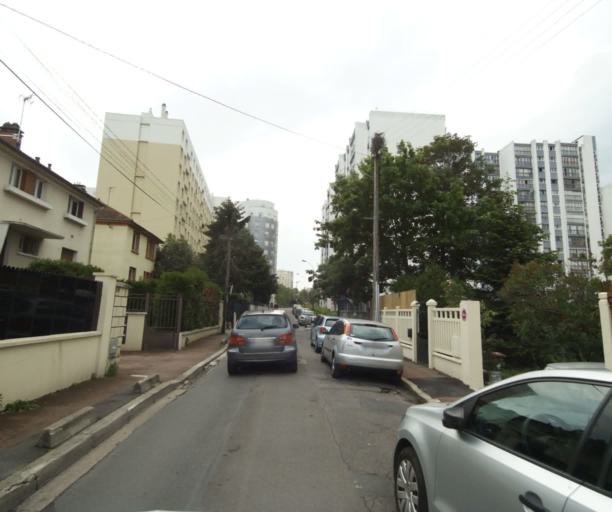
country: FR
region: Ile-de-France
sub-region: Departement du Val-d'Oise
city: Argenteuil
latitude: 48.9478
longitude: 2.2343
